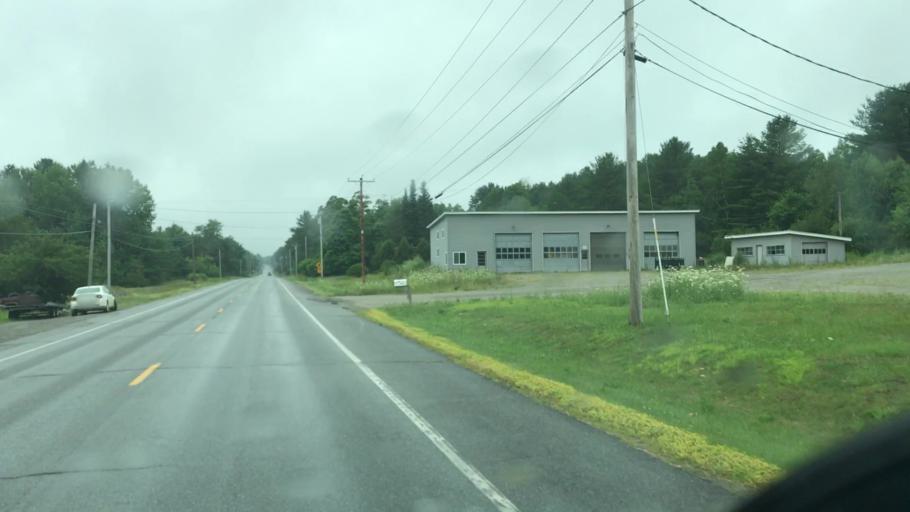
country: US
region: Maine
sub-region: Penobscot County
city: Lincoln
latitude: 45.3367
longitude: -68.5762
